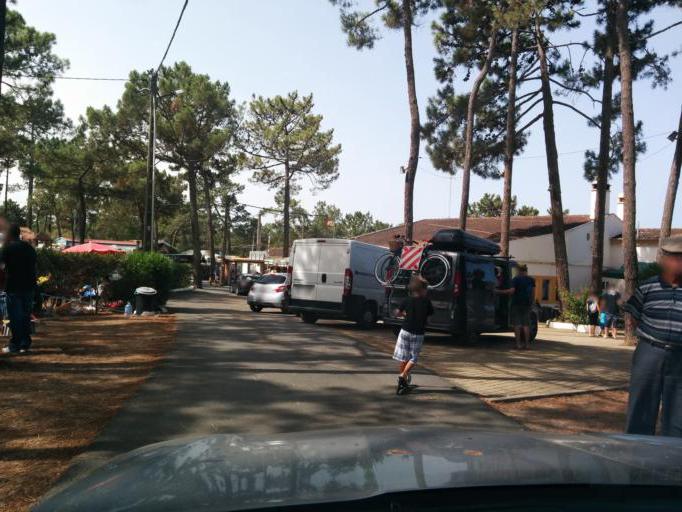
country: PT
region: Beja
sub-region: Odemira
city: Vila Nova de Milfontes
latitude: 37.7324
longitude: -8.7825
